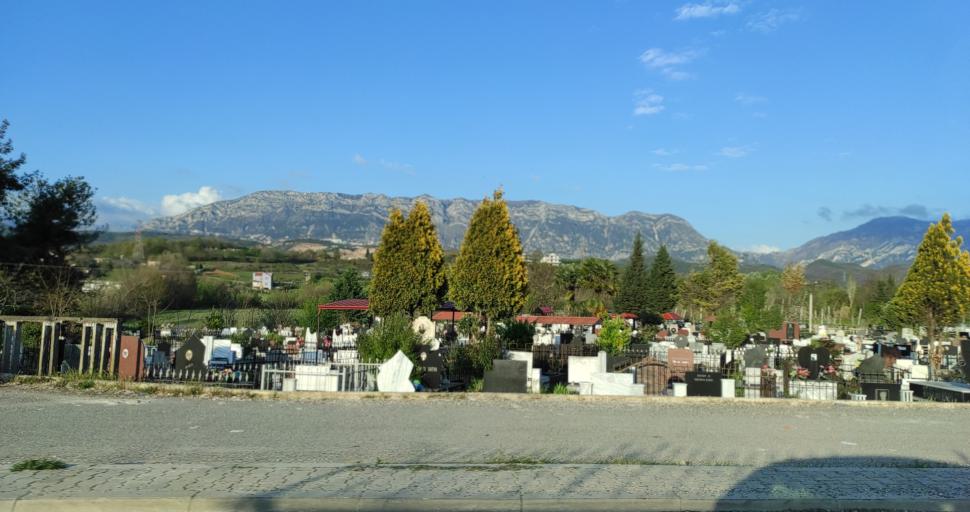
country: AL
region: Durres
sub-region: Rrethi i Krujes
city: Fushe-Kruje
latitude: 41.4828
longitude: 19.7343
